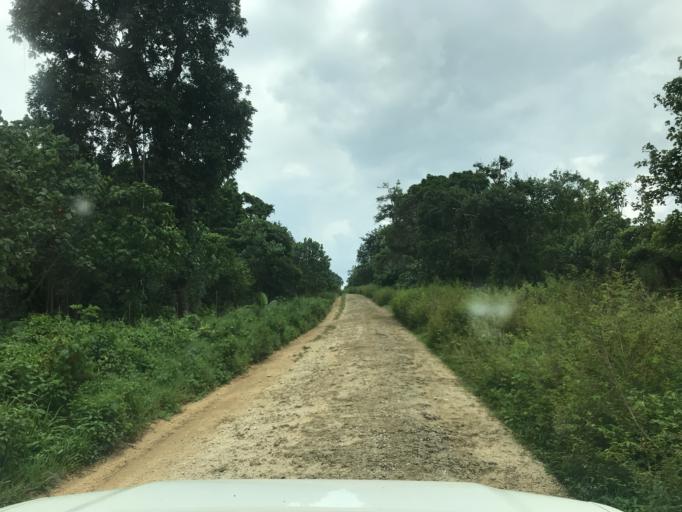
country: VU
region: Sanma
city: Port-Olry
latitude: -15.1870
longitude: 167.0042
